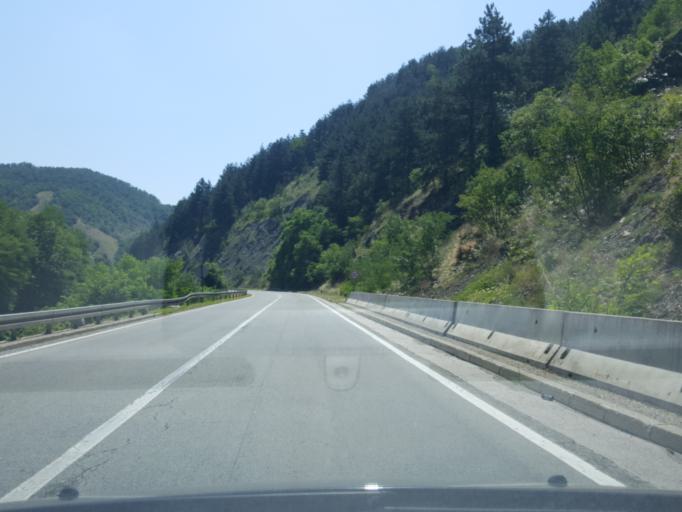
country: RS
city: Prislonica
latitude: 43.9867
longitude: 20.4181
